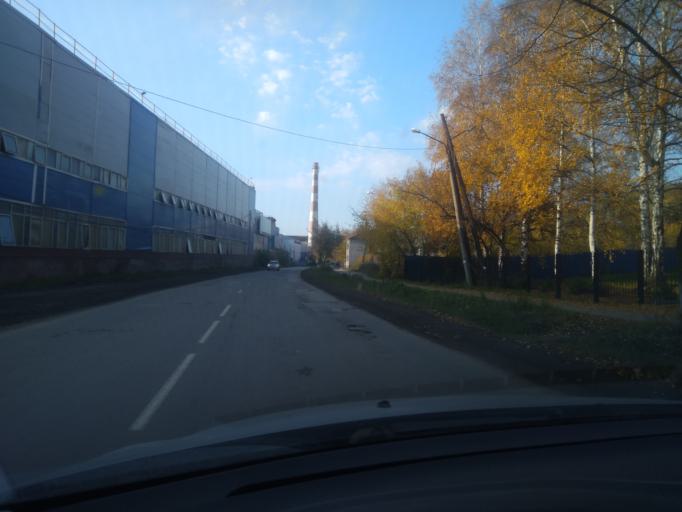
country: RU
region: Sverdlovsk
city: Nizhniye Sergi
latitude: 56.6665
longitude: 59.3139
